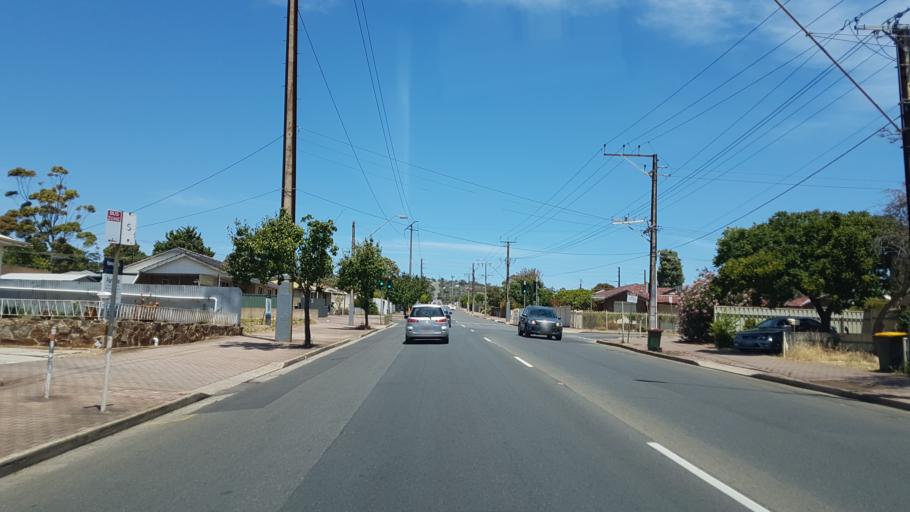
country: AU
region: South Australia
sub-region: Holdfast Bay
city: Seacliff Park
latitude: -35.0249
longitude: 138.5416
